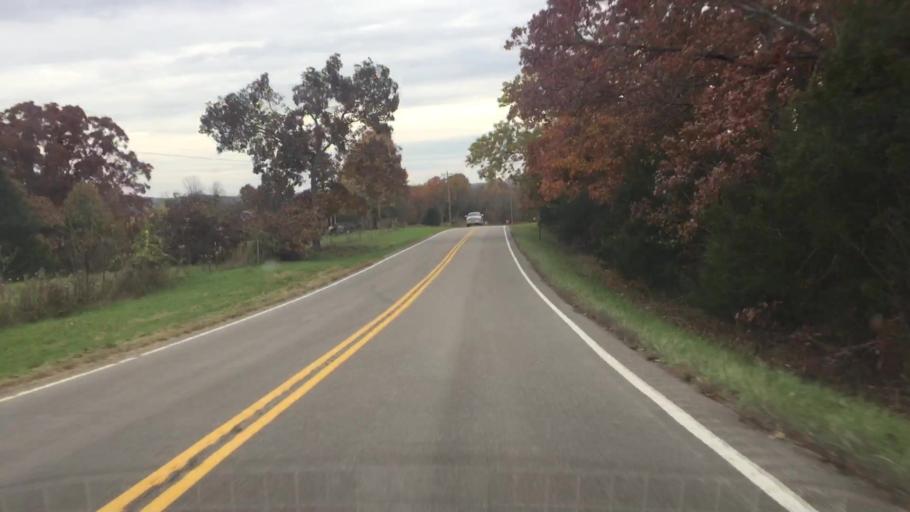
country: US
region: Missouri
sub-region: Gasconade County
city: Hermann
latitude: 38.7175
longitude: -91.7086
